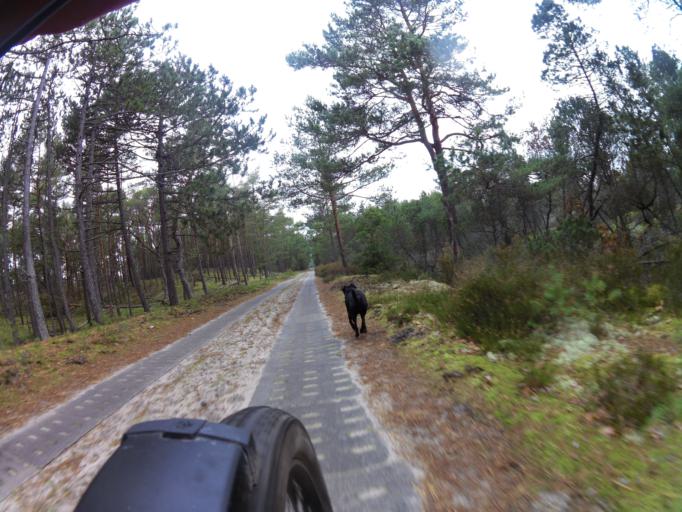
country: PL
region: Pomeranian Voivodeship
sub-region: Powiat pucki
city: Hel
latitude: 54.6253
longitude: 18.8162
